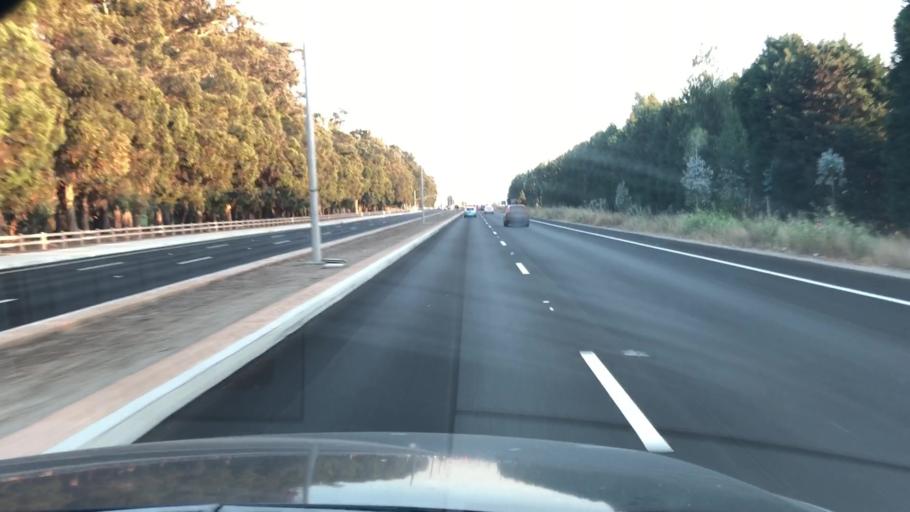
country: US
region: California
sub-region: Ventura County
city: Oxnard Shores
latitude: 34.2232
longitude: -119.2212
